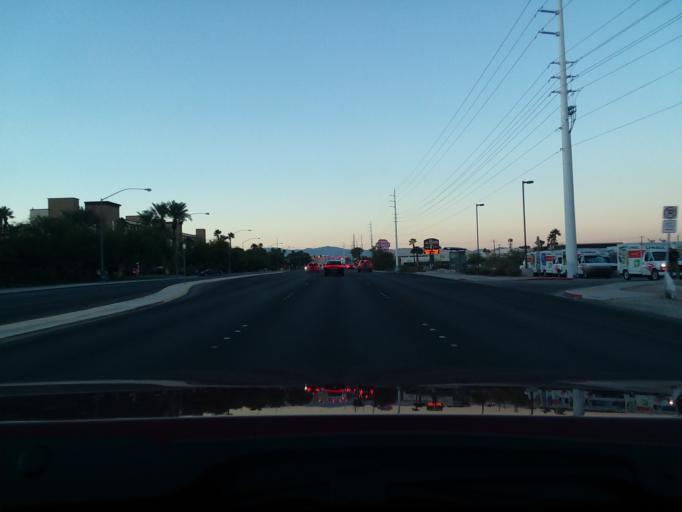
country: US
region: Nevada
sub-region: Clark County
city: Paradise
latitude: 36.0326
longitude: -115.1723
